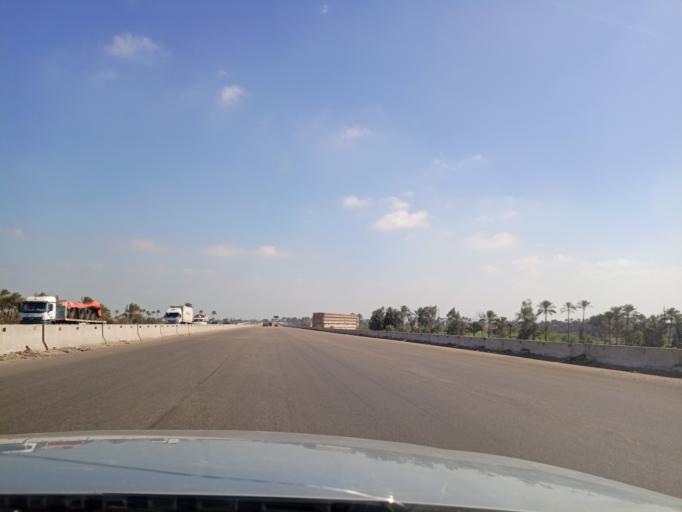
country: EG
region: Eastern Province
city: Mashtul as Suq
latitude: 30.4605
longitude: 31.3534
